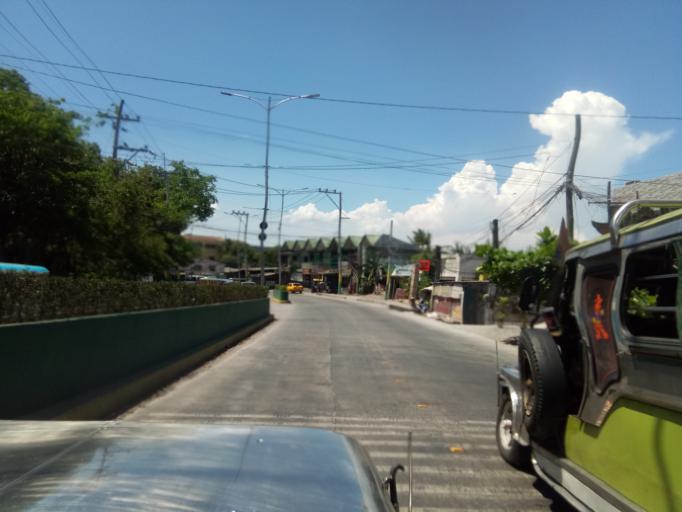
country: PH
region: Calabarzon
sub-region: Province of Cavite
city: Dasmarinas
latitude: 14.3227
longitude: 120.9636
